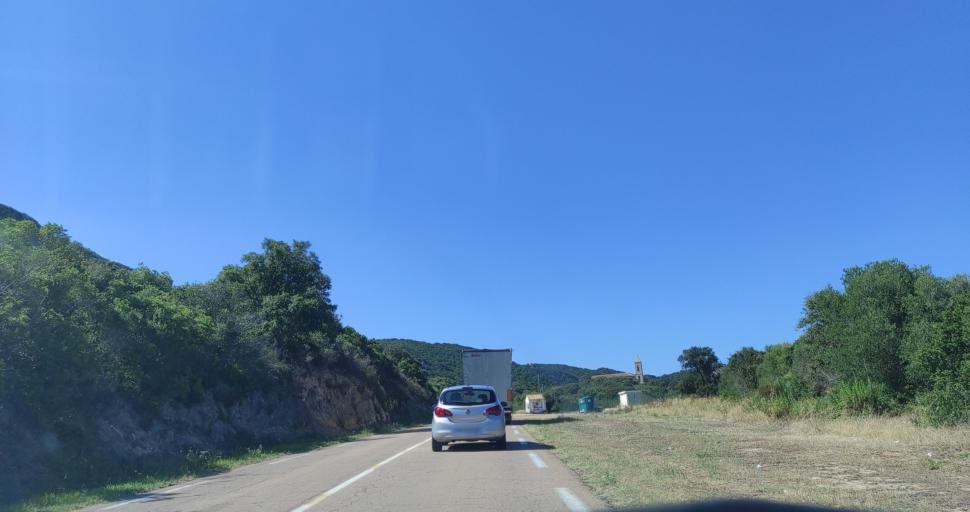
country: FR
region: Corsica
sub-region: Departement de la Corse-du-Sud
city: Bonifacio
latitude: 41.4936
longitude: 9.1335
